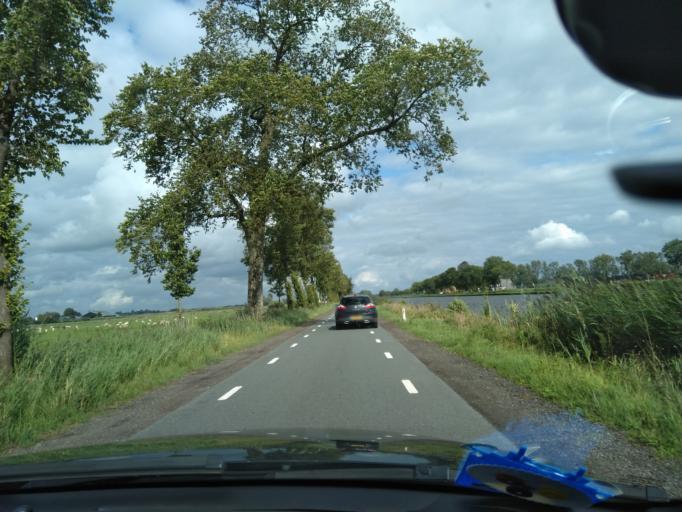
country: NL
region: Groningen
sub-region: Gemeente Zuidhorn
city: Grijpskerk
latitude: 53.2524
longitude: 6.3418
